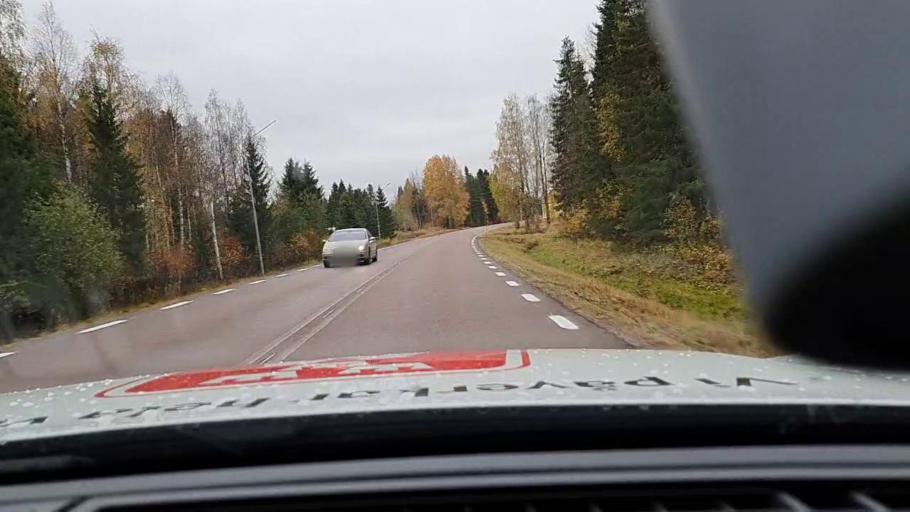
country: FI
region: Lapland
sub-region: Torniolaakso
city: Ylitornio
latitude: 66.1458
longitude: 23.8941
